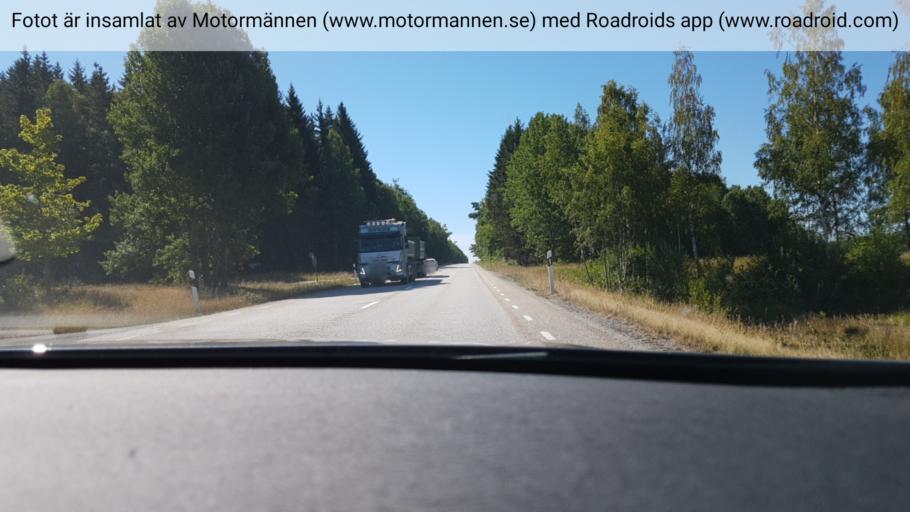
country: SE
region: Joenkoeping
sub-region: Habo Kommun
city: Habo
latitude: 57.9073
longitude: 14.1041
